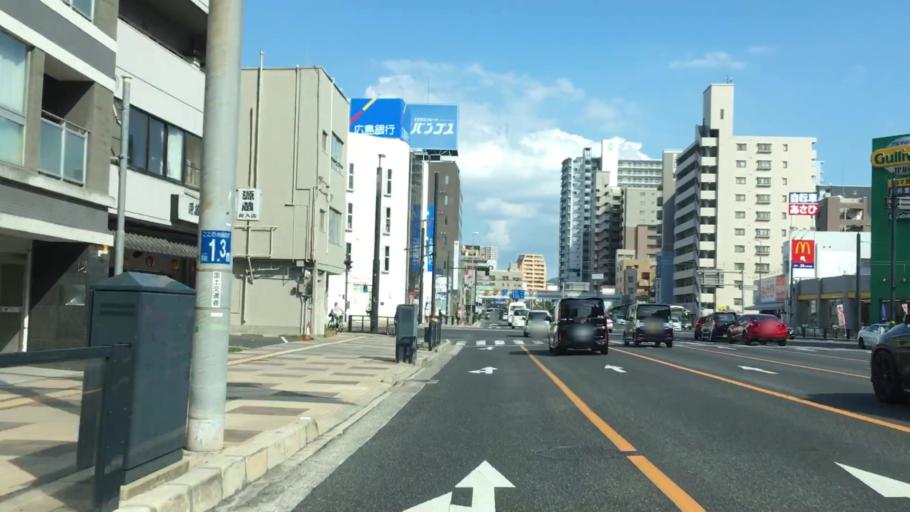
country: JP
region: Hiroshima
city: Hiroshima-shi
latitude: 34.3866
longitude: 132.4425
